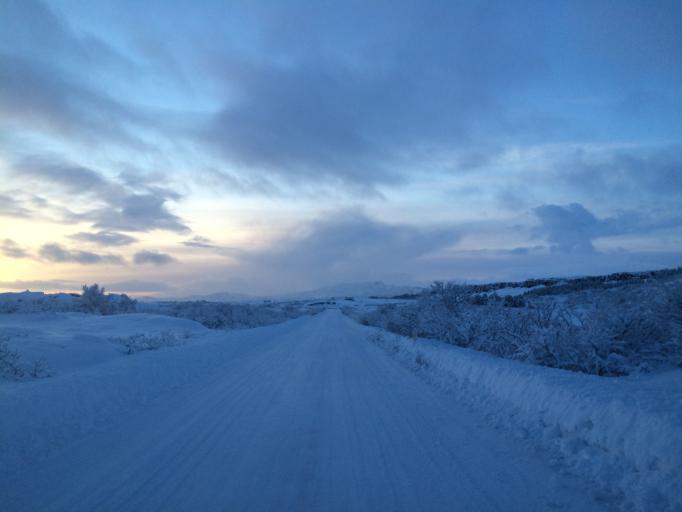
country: IS
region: South
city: Hveragerdi
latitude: 64.2722
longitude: -21.1030
